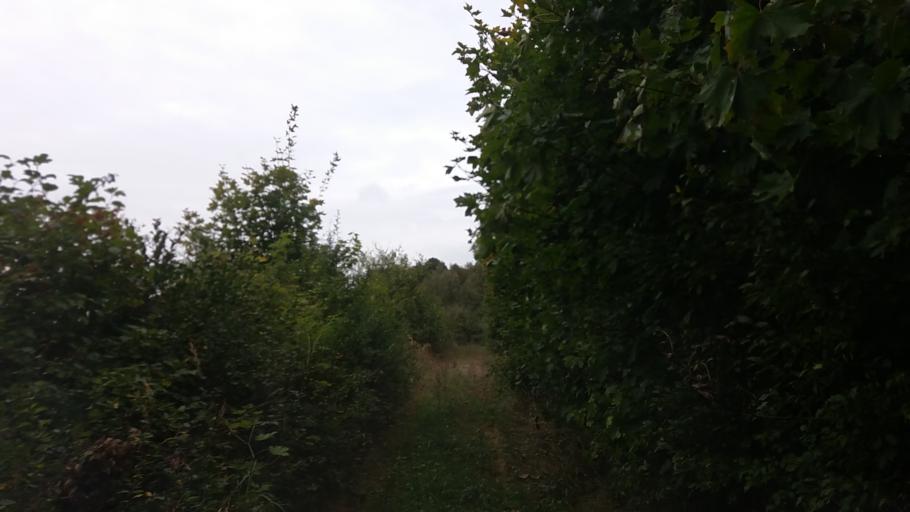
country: PL
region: West Pomeranian Voivodeship
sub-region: Powiat choszczenski
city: Bierzwnik
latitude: 52.9925
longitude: 15.6036
